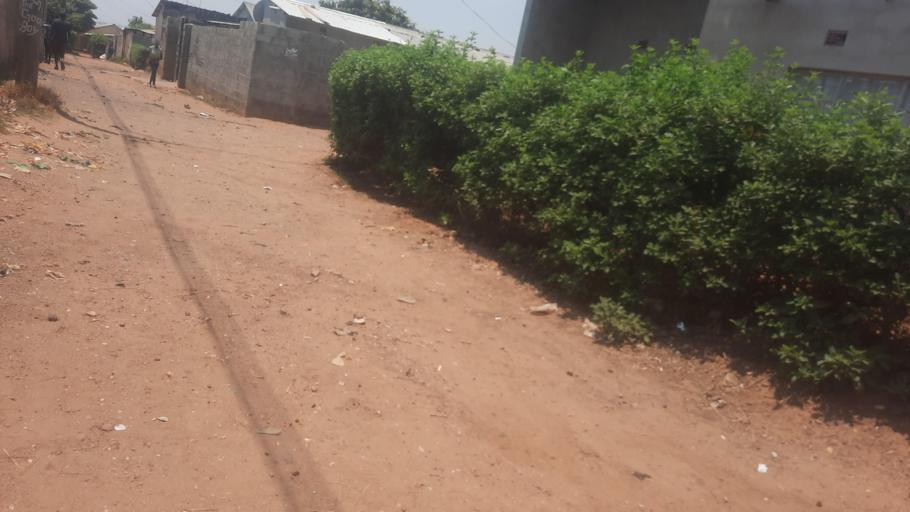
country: ZM
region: Lusaka
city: Lusaka
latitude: -15.4022
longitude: 28.3704
